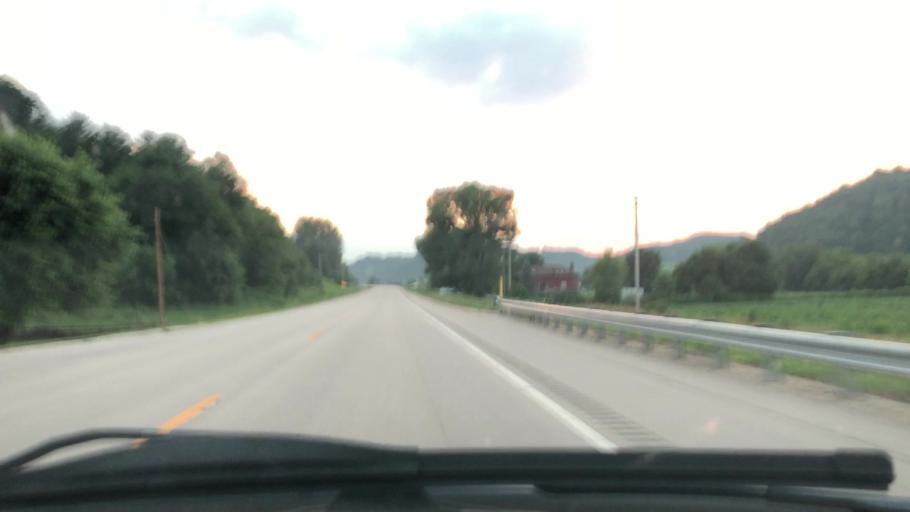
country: US
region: Wisconsin
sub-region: Richland County
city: Richland Center
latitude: 43.3475
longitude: -90.4181
